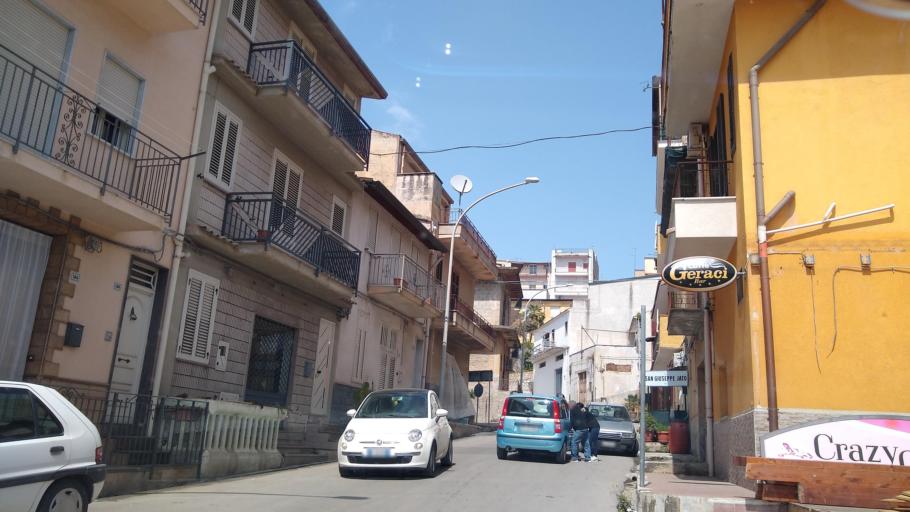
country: IT
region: Sicily
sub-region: Palermo
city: San Cipirello
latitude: 37.9679
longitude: 13.1786
